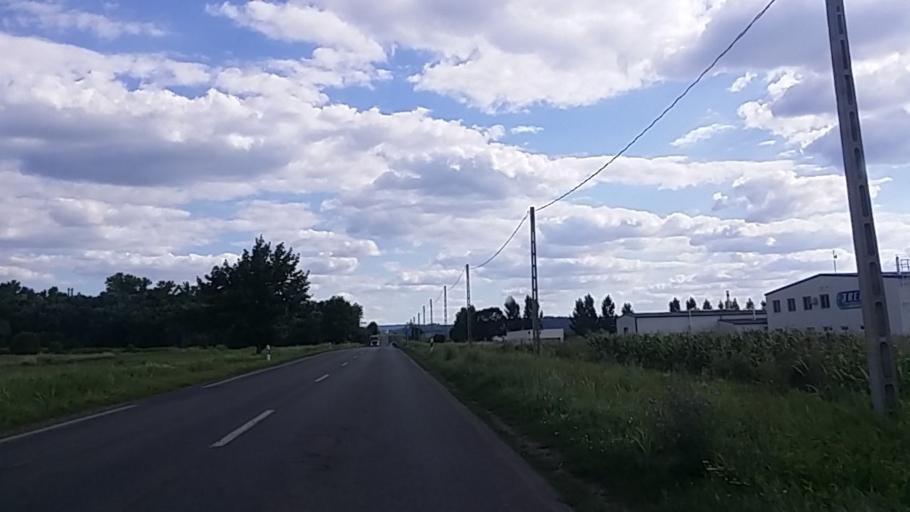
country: HU
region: Baranya
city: Sasd
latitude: 46.2415
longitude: 18.1209
